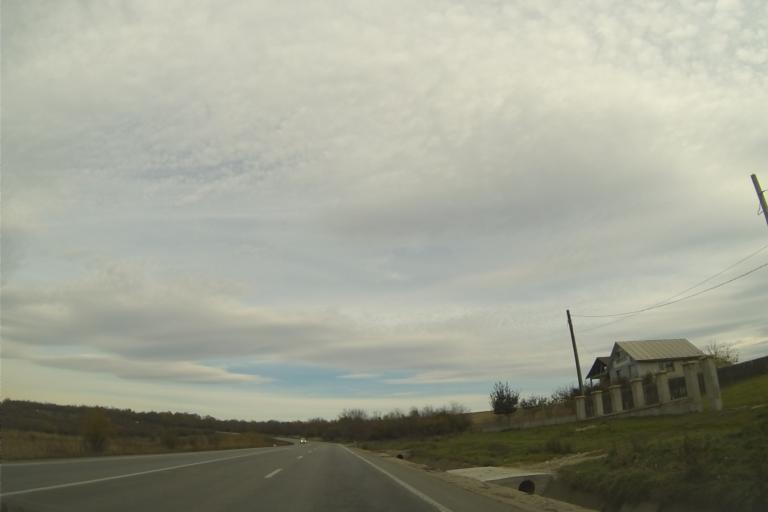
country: RO
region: Olt
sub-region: Comuna Valea Mare
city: Valea Mare
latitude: 44.4832
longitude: 24.4407
